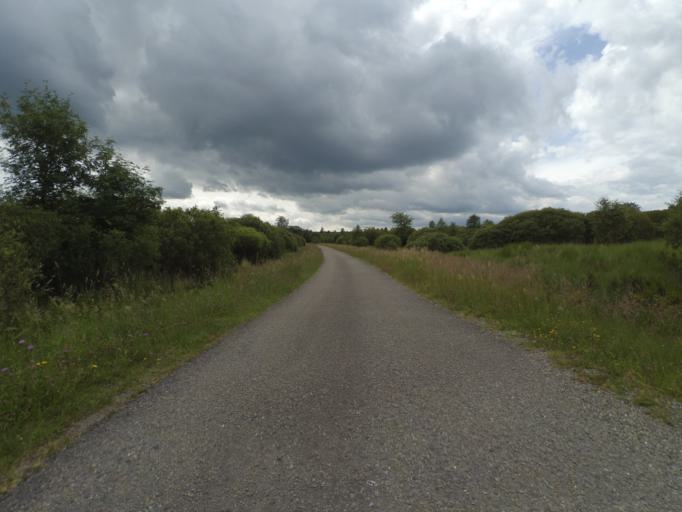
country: DE
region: North Rhine-Westphalia
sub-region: Regierungsbezirk Koln
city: Monschau
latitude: 50.5725
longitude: 6.1789
